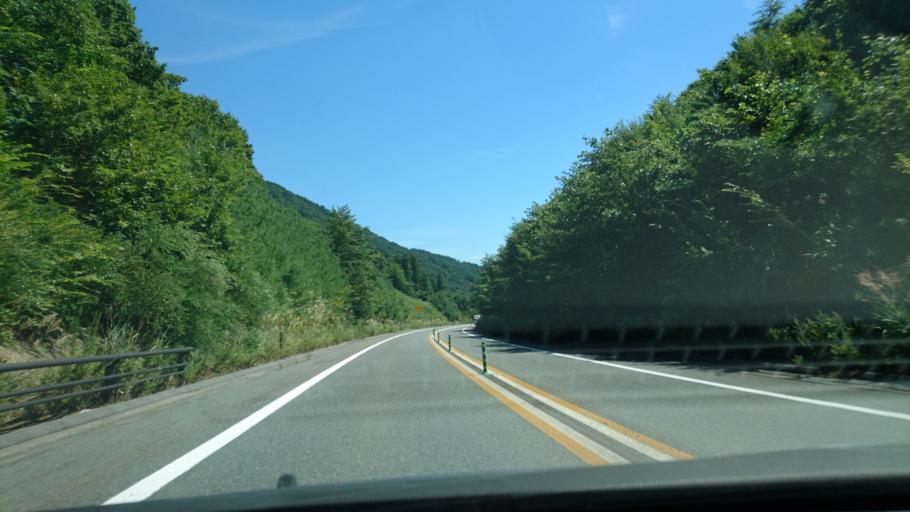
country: JP
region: Iwate
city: Kamaishi
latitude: 39.2509
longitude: 141.7494
